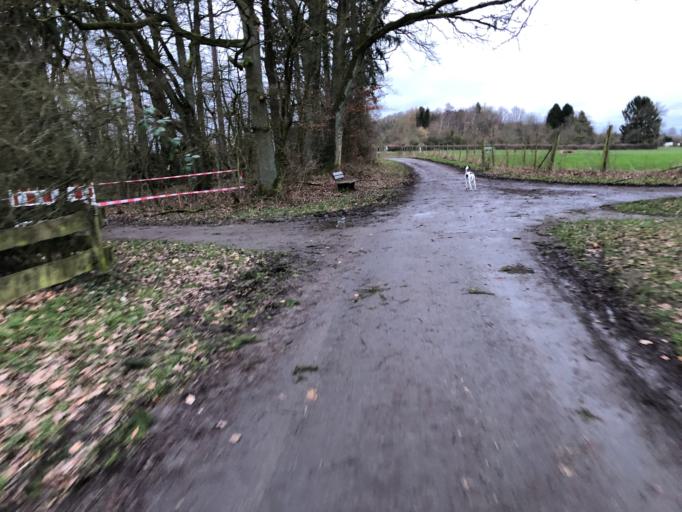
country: DE
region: North Rhine-Westphalia
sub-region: Regierungsbezirk Detmold
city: Detmold
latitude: 51.9279
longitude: 8.8618
